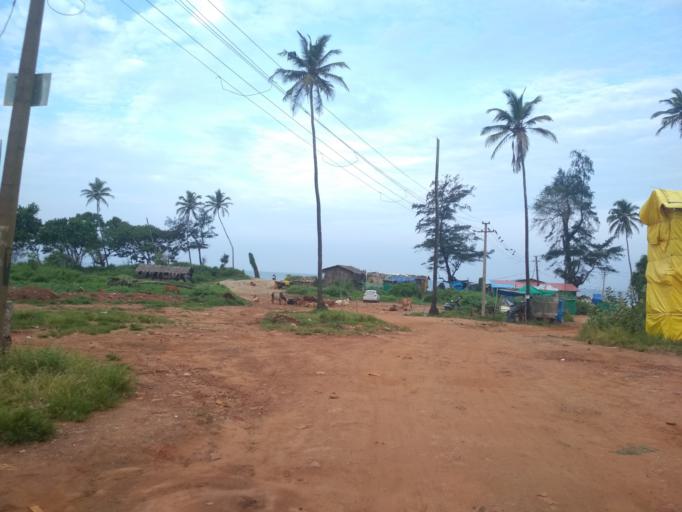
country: IN
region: Goa
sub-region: North Goa
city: Arambol
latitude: 15.6875
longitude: 73.7046
